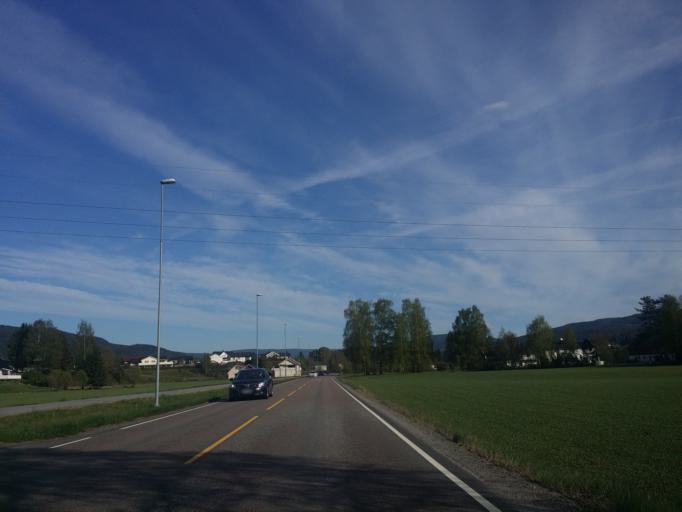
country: NO
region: Telemark
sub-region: Notodden
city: Notodden
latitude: 59.5954
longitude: 9.1406
